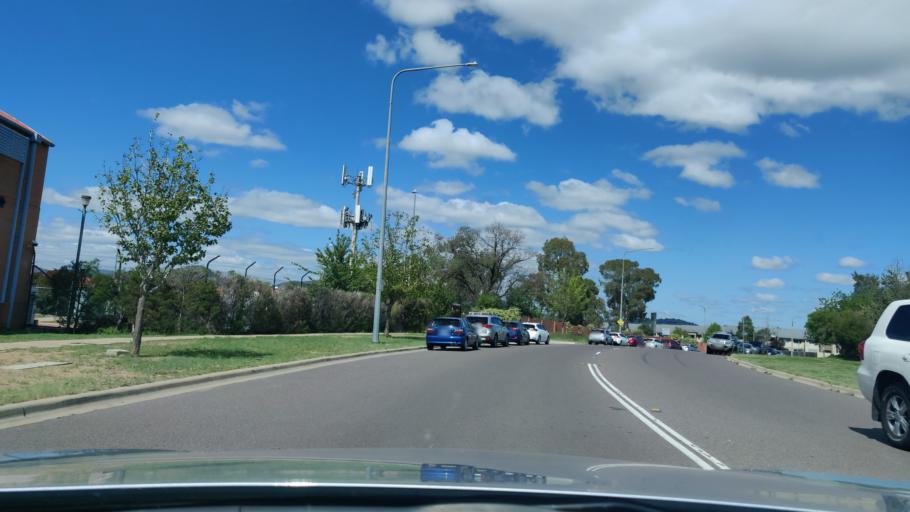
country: AU
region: Australian Capital Territory
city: Macarthur
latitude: -35.4234
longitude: 149.0703
